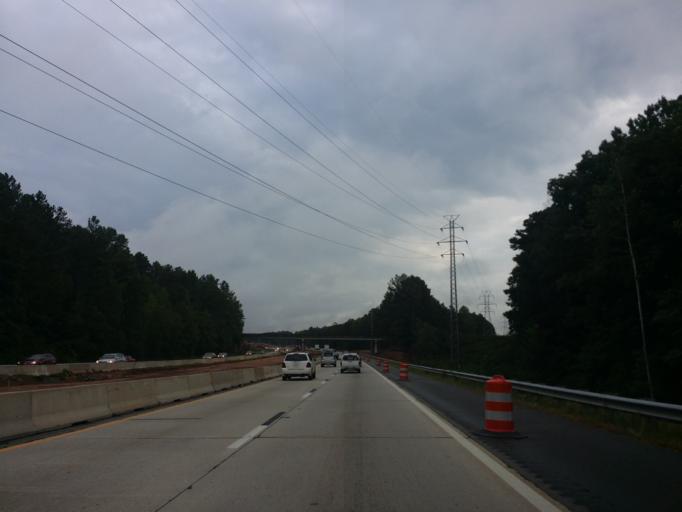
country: US
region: North Carolina
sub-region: Durham County
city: Durham
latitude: 35.9544
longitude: -78.8639
